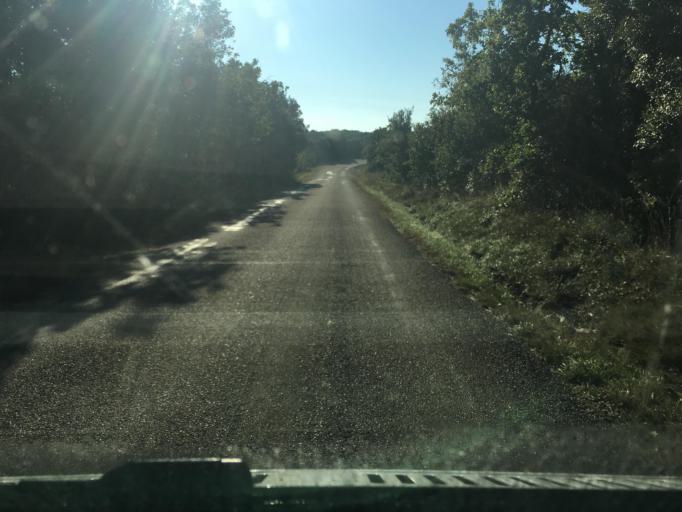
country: FR
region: Languedoc-Roussillon
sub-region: Departement du Gard
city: Goudargues
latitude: 44.1716
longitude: 4.3459
